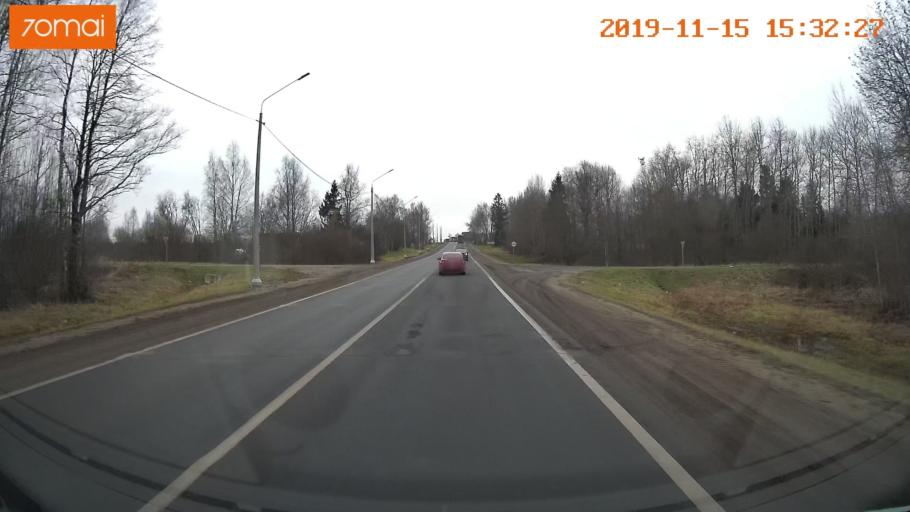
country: RU
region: Jaroslavl
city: Danilov
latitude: 58.0901
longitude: 40.1000
